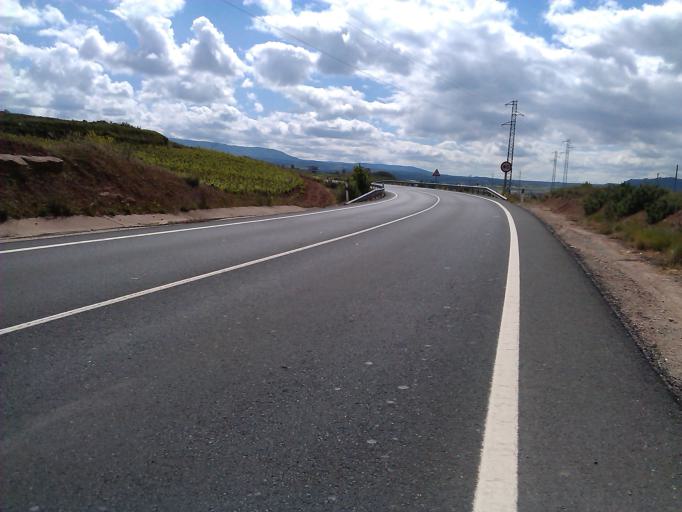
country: ES
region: La Rioja
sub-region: Provincia de La Rioja
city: Hormilla
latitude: 42.4295
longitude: -2.7561
